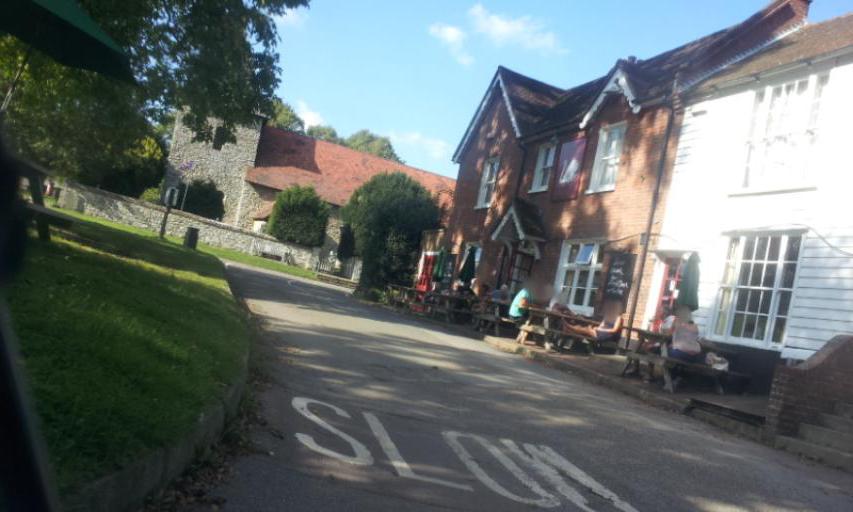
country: GB
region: England
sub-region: Kent
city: Hadlow
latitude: 51.2481
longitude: 0.3546
